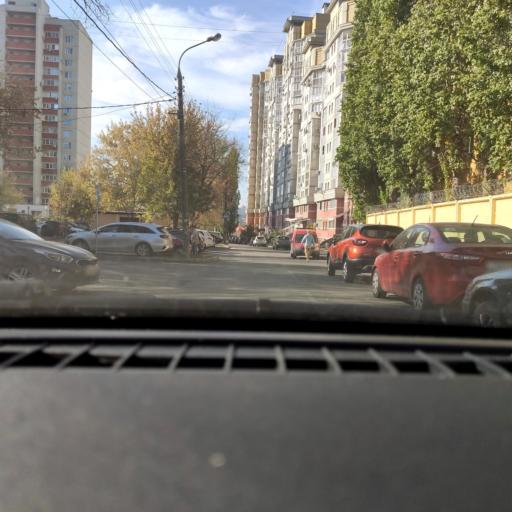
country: RU
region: Voronezj
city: Voronezh
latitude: 51.6748
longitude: 39.2471
